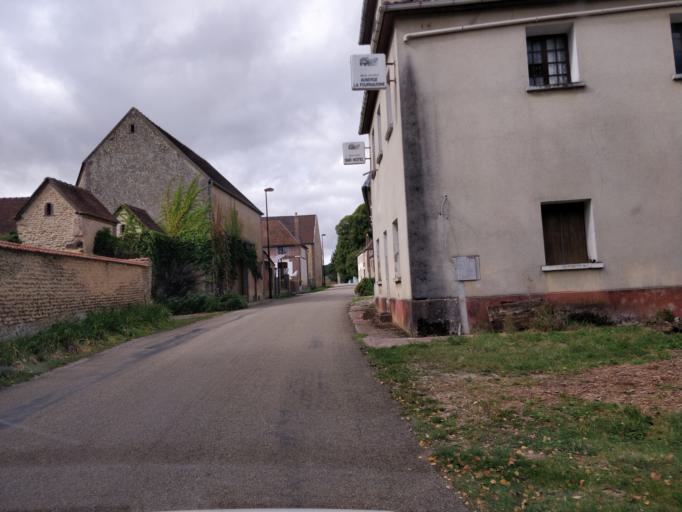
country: FR
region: Champagne-Ardenne
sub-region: Departement de l'Aube
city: Aix-en-Othe
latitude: 48.1543
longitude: 3.6404
